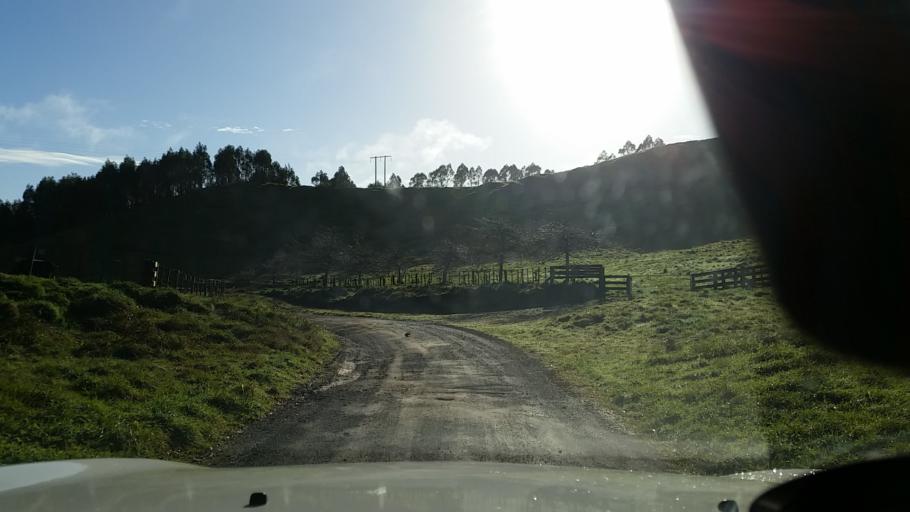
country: NZ
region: Bay of Plenty
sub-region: Kawerau District
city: Kawerau
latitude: -38.0173
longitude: 176.5977
